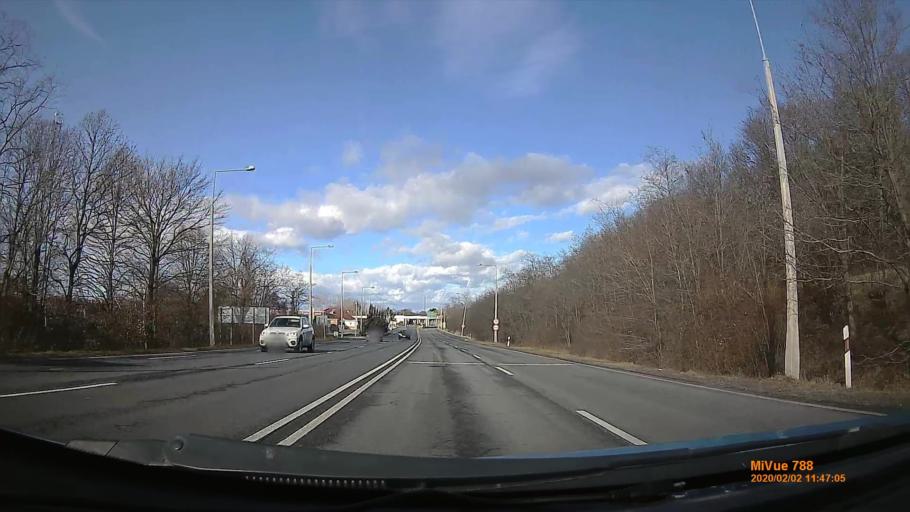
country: AT
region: Burgenland
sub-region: Eisenstadt-Umgebung
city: Klingenbach
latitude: 47.7372
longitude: 16.5489
